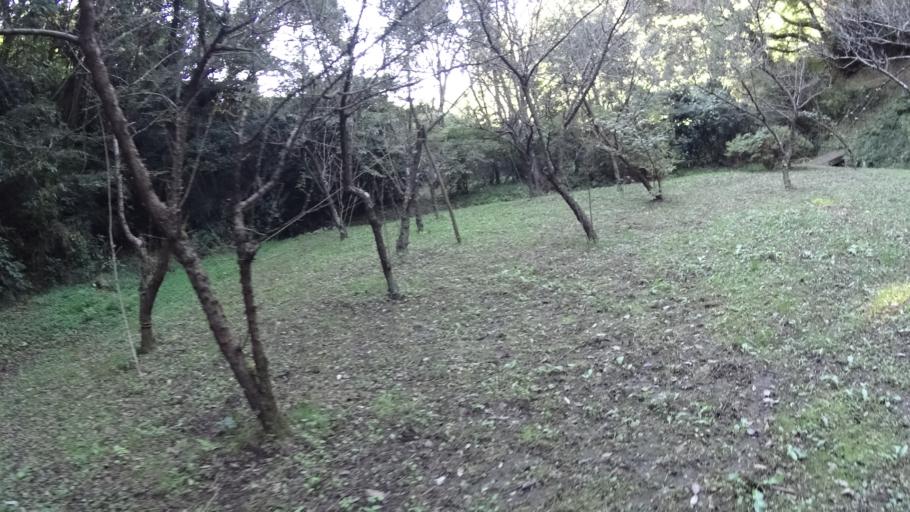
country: JP
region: Kanagawa
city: Kamakura
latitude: 35.3655
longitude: 139.6011
